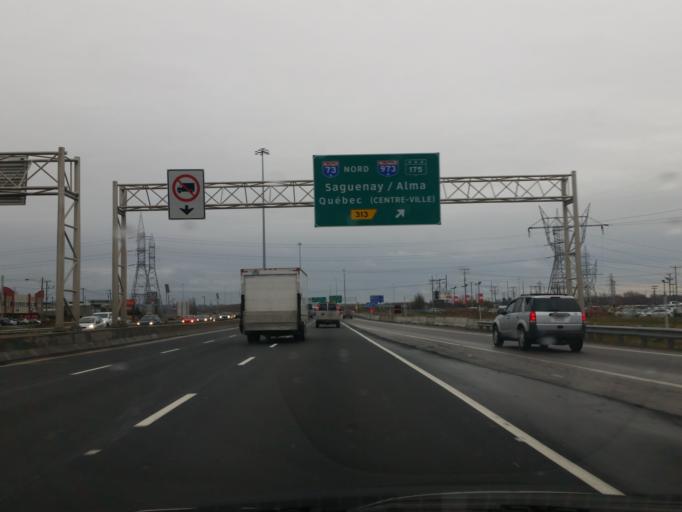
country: CA
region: Quebec
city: Quebec
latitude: 46.8330
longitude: -71.2736
